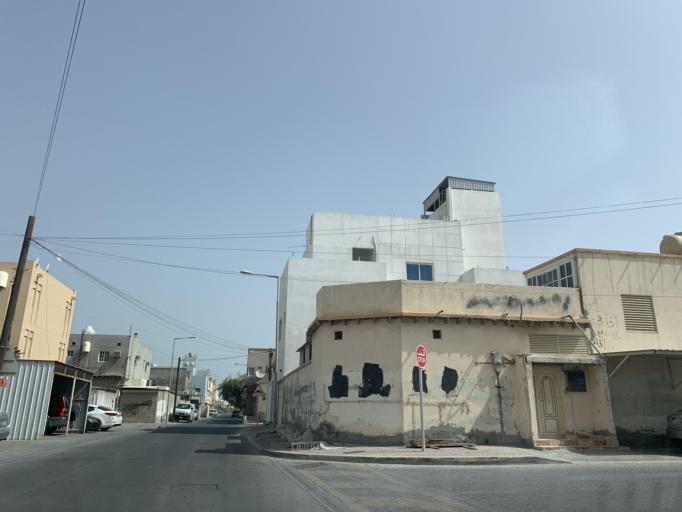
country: BH
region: Northern
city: Sitrah
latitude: 26.1370
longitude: 50.5997
